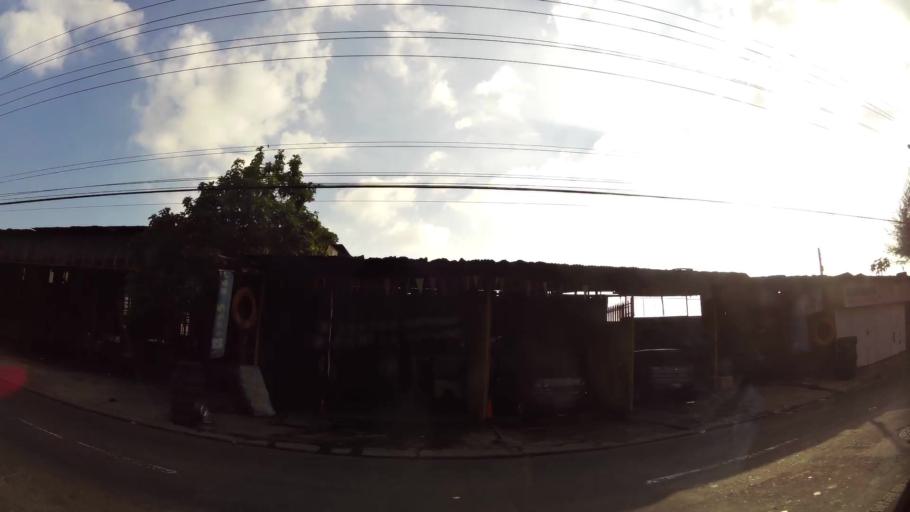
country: SV
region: San Salvador
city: San Salvador
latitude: 13.6937
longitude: -89.2229
